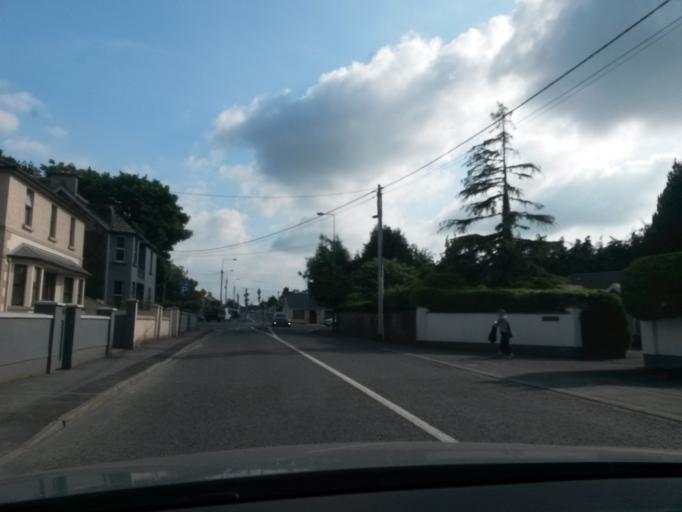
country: IE
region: Munster
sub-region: An Clar
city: Ennis
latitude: 52.8409
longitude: -8.9773
